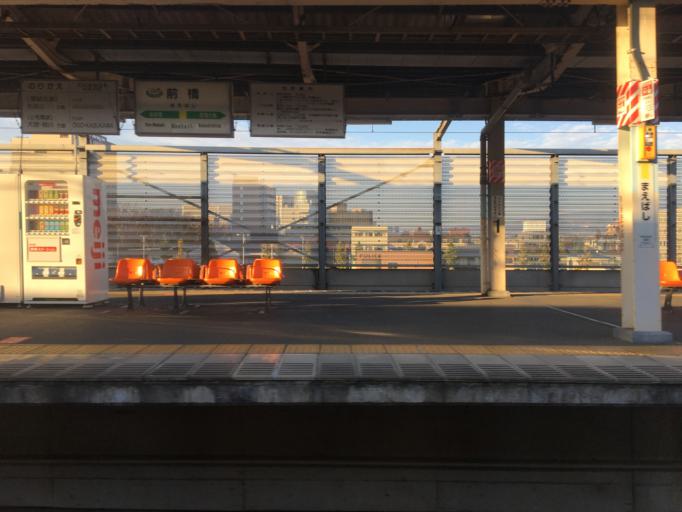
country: JP
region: Gunma
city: Maebashi-shi
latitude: 36.3834
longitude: 139.0738
